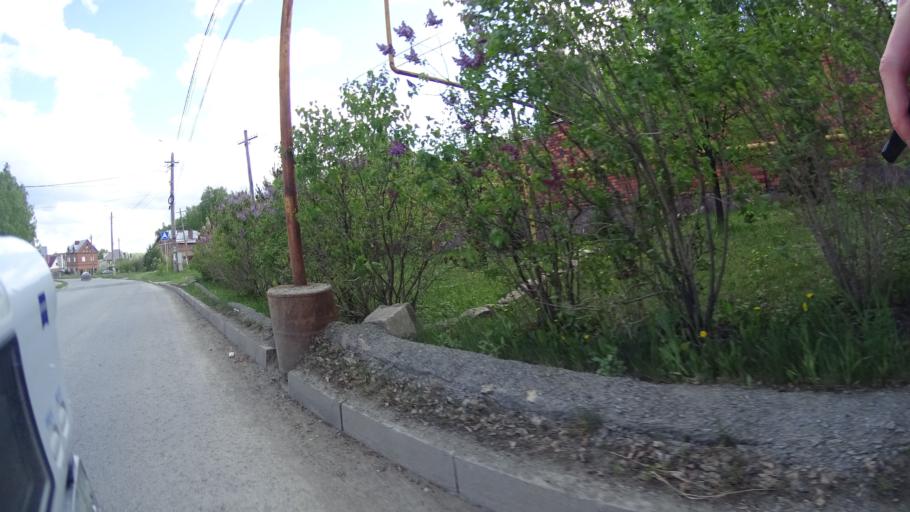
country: RU
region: Chelyabinsk
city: Sargazy
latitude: 55.1569
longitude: 61.2518
